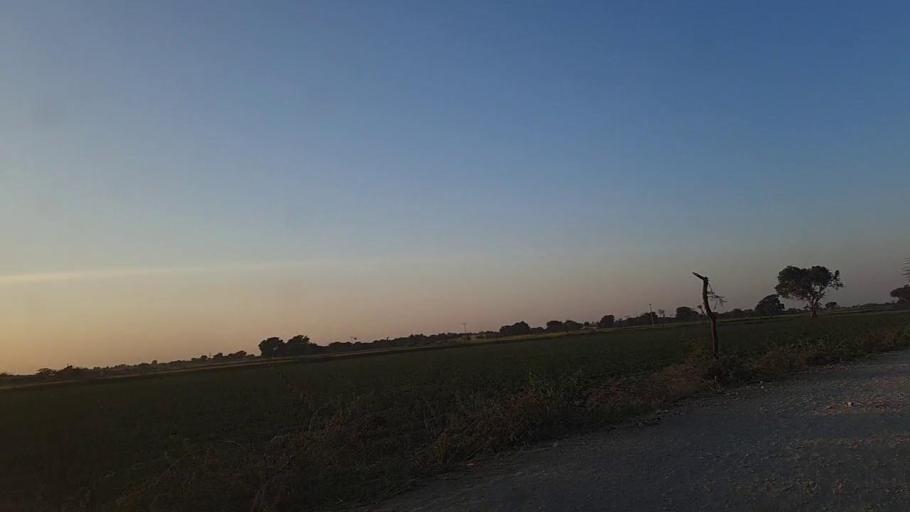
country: PK
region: Sindh
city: Naukot
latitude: 25.0476
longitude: 69.4071
